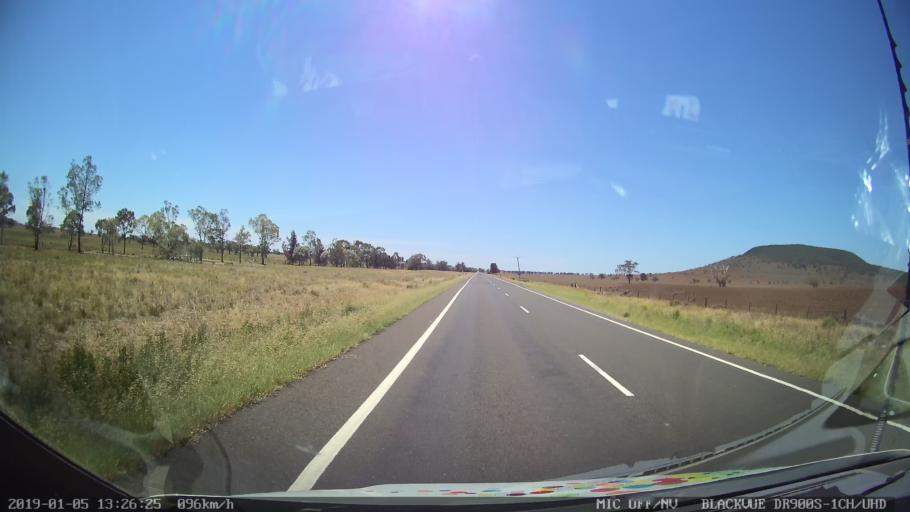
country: AU
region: New South Wales
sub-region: Gunnedah
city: Gunnedah
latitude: -31.0531
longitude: 150.0154
